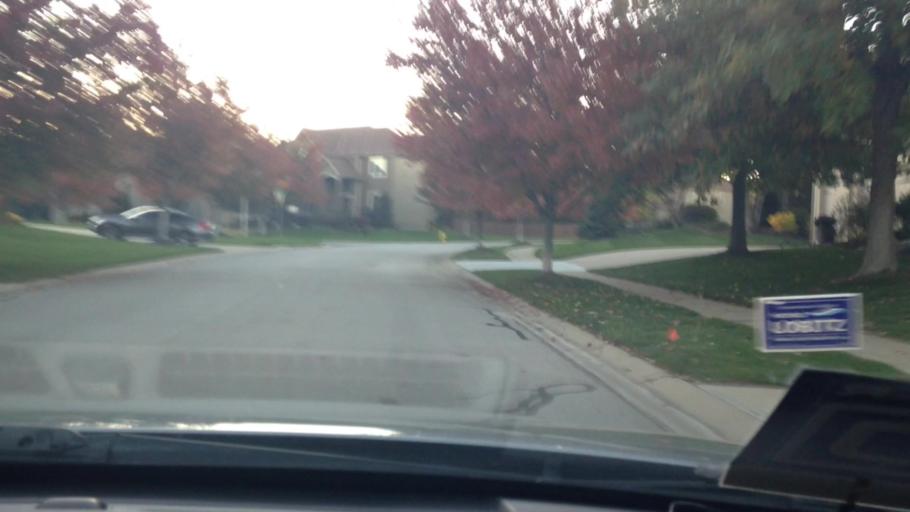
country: US
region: Kansas
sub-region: Johnson County
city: Lenexa
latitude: 38.8636
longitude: -94.7182
